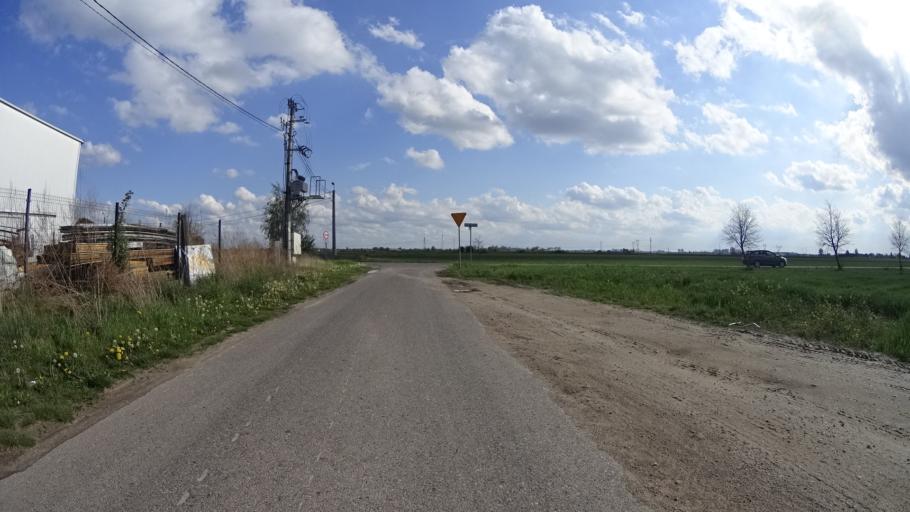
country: PL
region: Masovian Voivodeship
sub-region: Powiat warszawski zachodni
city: Jozefow
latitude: 52.2350
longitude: 20.6741
